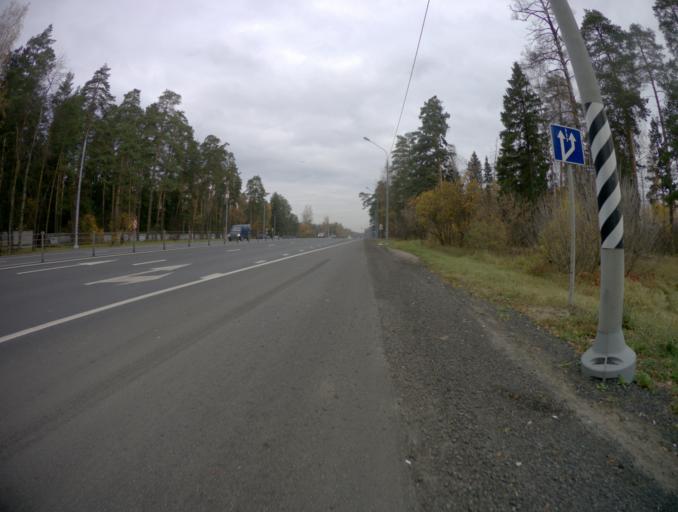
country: RU
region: Moskovskaya
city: Malaya Dubna
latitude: 55.8464
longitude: 38.9649
